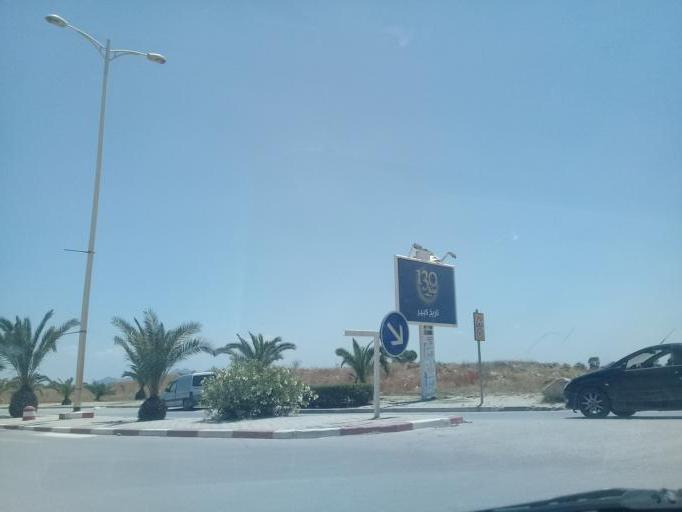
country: TN
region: Tunis
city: La Goulette
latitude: 36.8423
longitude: 10.2663
